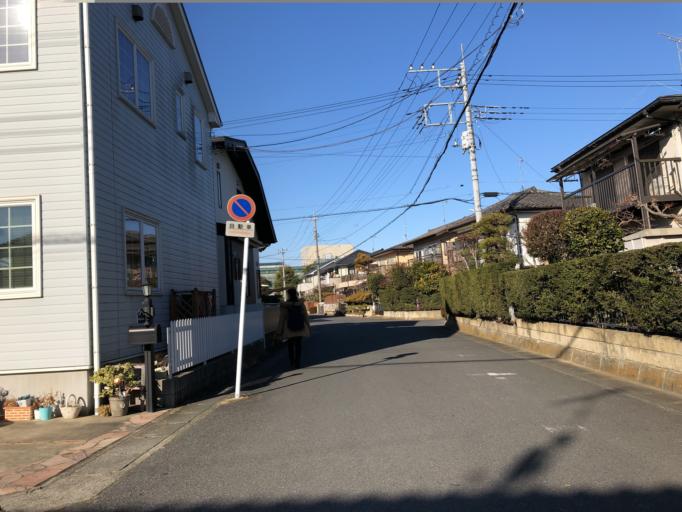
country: JP
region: Saitama
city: Sugito
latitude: 36.0265
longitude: 139.7175
